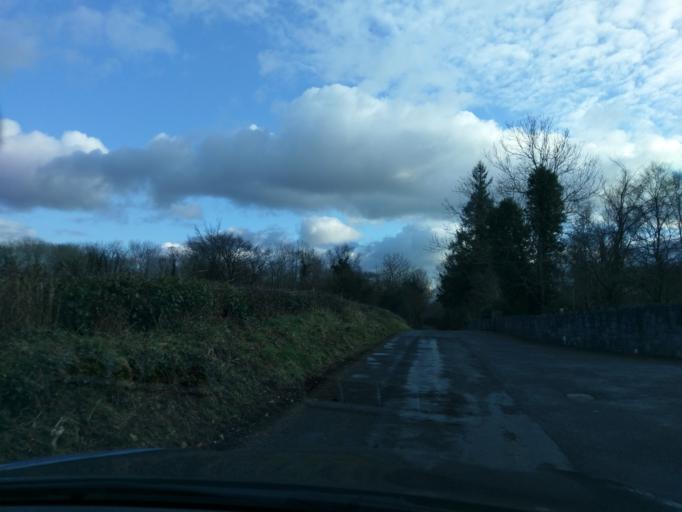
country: IE
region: Connaught
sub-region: County Galway
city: Athenry
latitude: 53.3623
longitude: -8.6474
